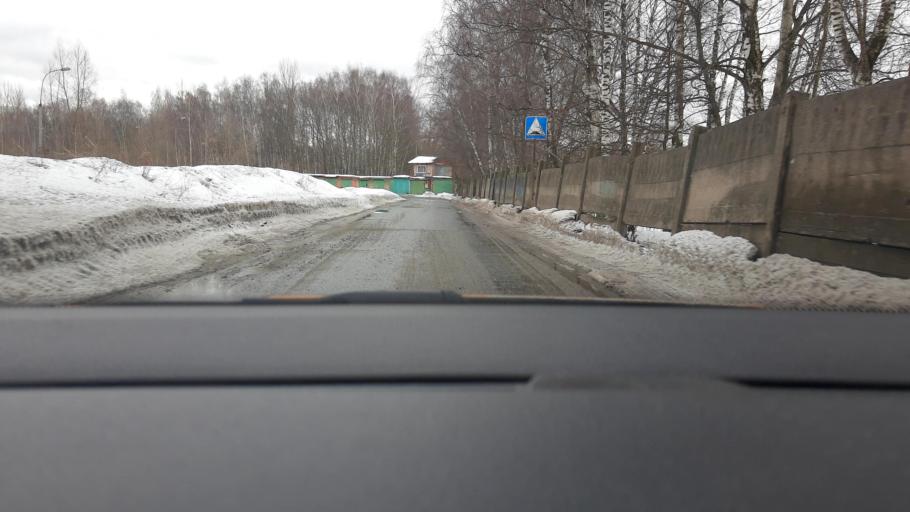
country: RU
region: Moscow
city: Babushkin
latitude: 55.8512
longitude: 37.7014
